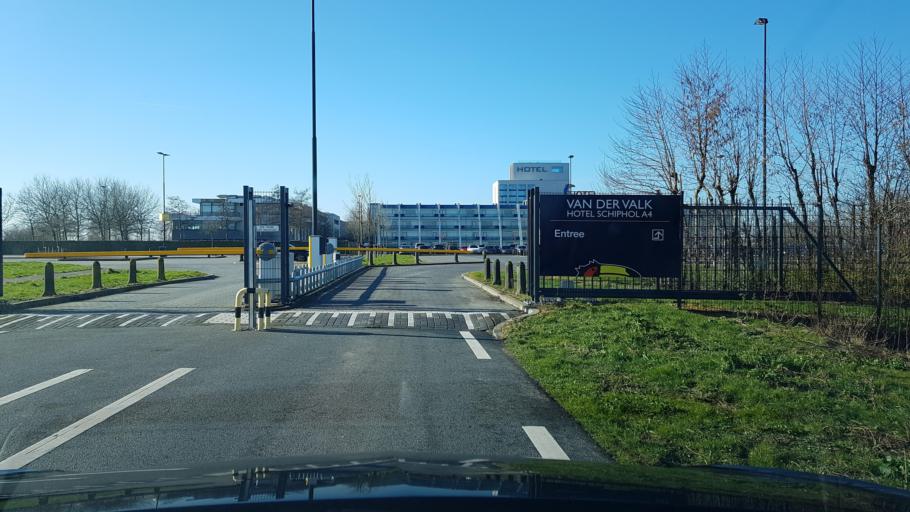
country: NL
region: North Holland
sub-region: Gemeente Haarlemmermeer
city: Hoofddorp
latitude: 52.2602
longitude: 4.6920
